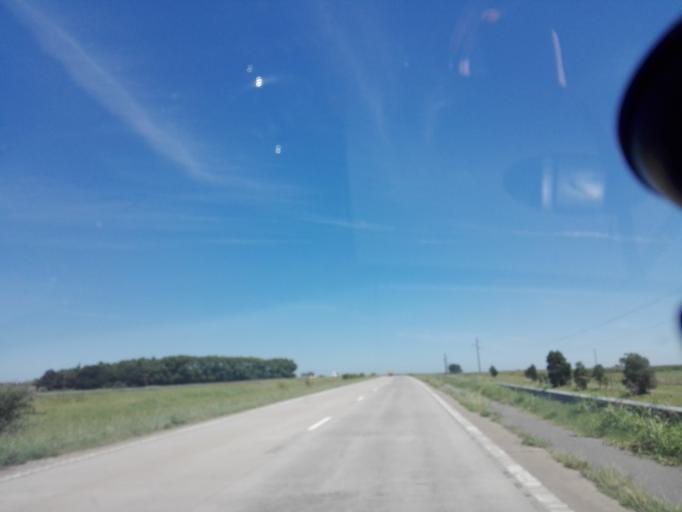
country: AR
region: Santa Fe
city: Canada de Gomez
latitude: -32.8433
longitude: -61.4093
